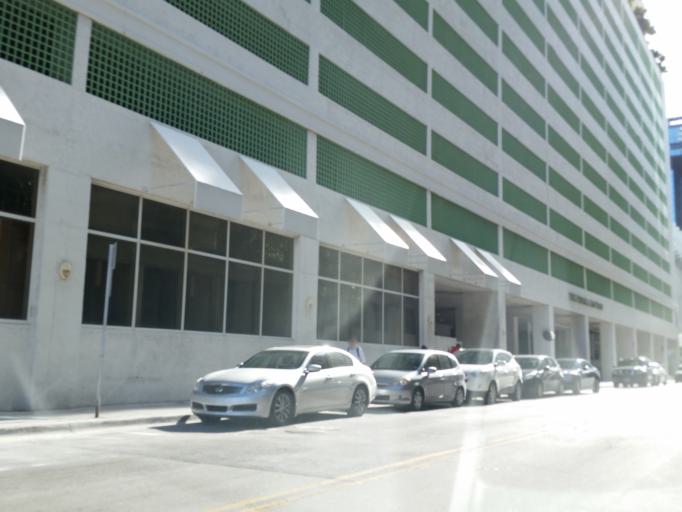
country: US
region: Florida
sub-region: Miami-Dade County
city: Miami
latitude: 25.7619
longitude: -80.1900
